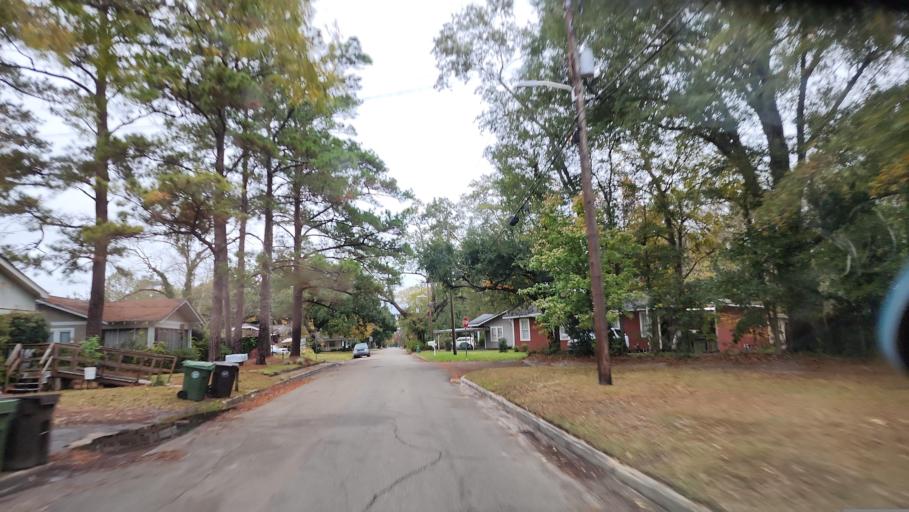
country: US
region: Mississippi
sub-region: Forrest County
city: Hattiesburg
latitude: 31.3183
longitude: -89.3057
